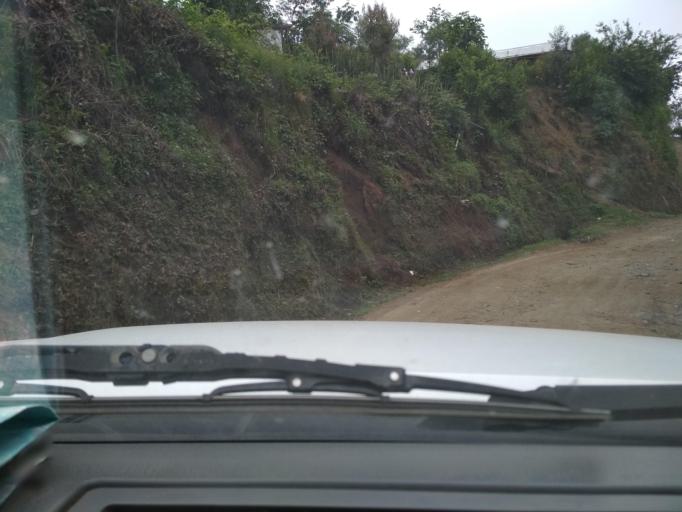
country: MX
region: Veracruz
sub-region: La Perla
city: Chilapa
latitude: 18.9989
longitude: -97.1662
